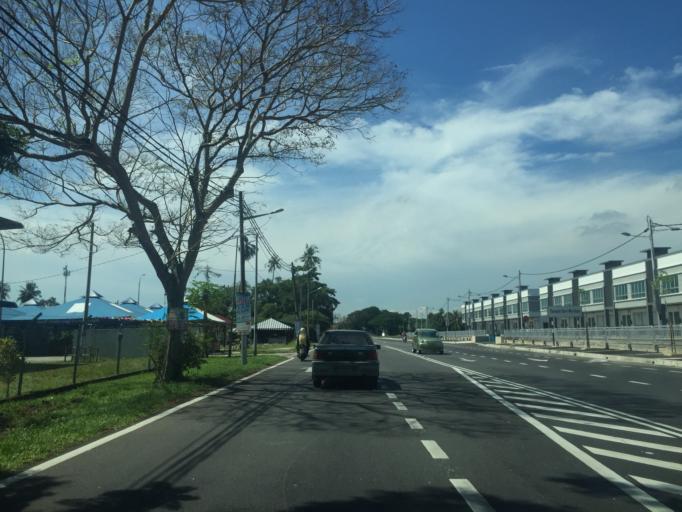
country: MY
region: Penang
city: Permatang Kuching
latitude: 5.4550
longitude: 100.4407
